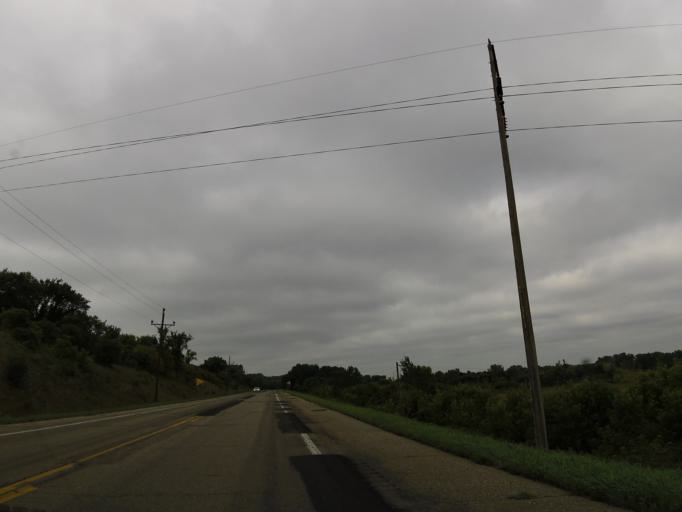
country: US
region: Minnesota
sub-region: Yellow Medicine County
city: Granite Falls
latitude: 44.8335
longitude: -95.6077
